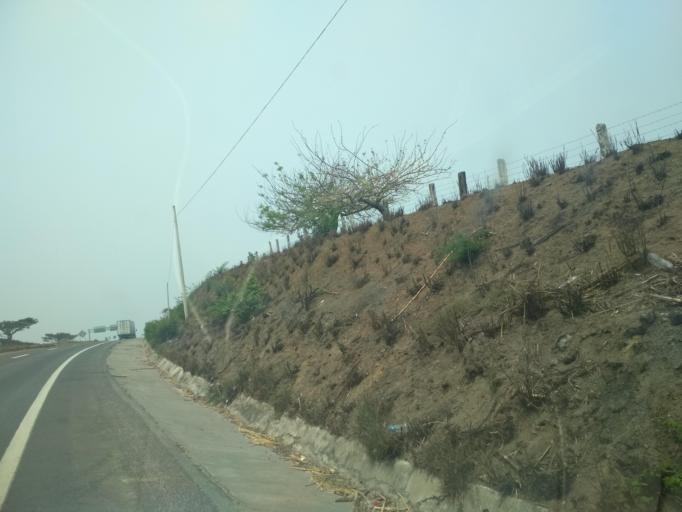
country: MX
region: Veracruz
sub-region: Veracruz
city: Delfino Victoria (Santa Fe)
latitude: 19.1961
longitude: -96.2745
